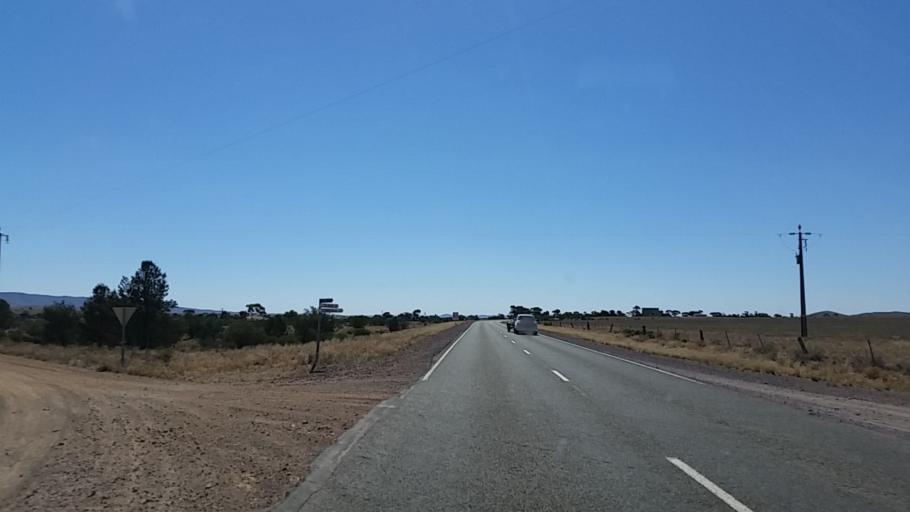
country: AU
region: South Australia
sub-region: Flinders Ranges
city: Quorn
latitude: -32.4333
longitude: 138.5330
